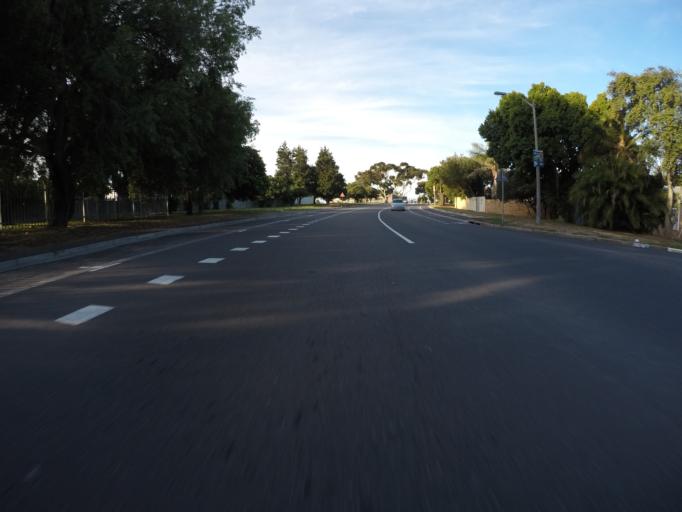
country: ZA
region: Western Cape
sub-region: City of Cape Town
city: Kraaifontein
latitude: -33.8681
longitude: 18.6513
